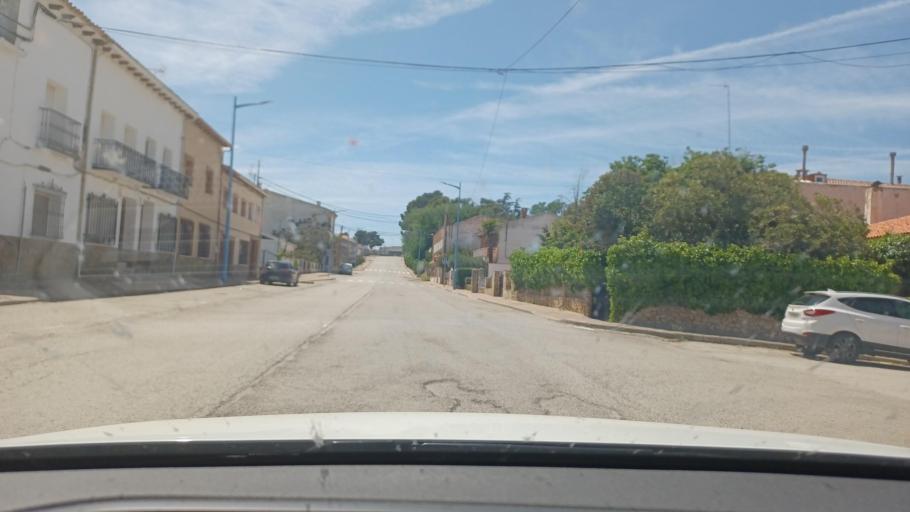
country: ES
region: Castille-La Mancha
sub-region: Provincia de Cuenca
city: Montalbo
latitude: 39.8816
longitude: -2.6696
